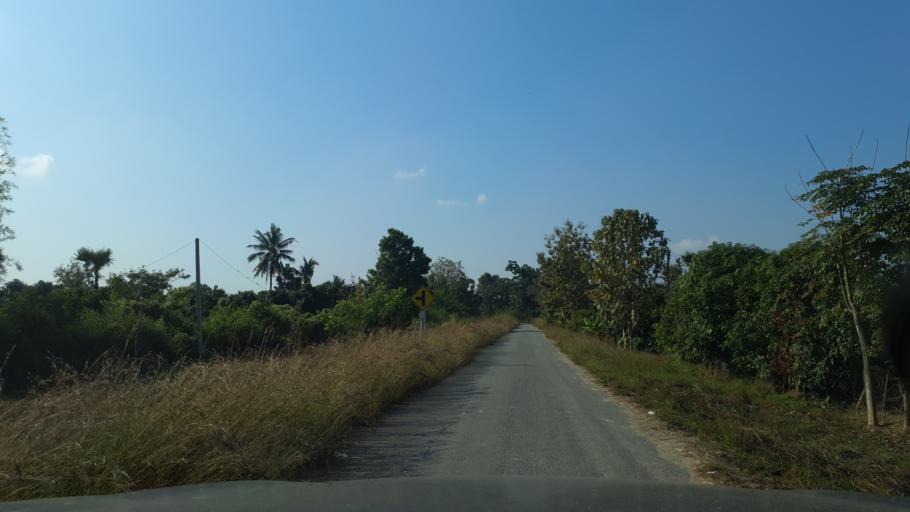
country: TH
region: Lamphun
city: Ban Thi
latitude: 18.6700
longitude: 99.1332
